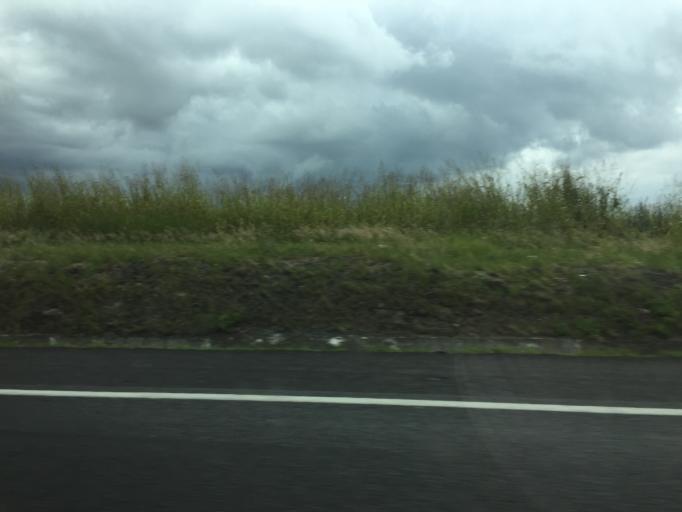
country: MX
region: Jalisco
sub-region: Zapotlanejo
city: La Mezquitera
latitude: 20.5821
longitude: -103.0949
